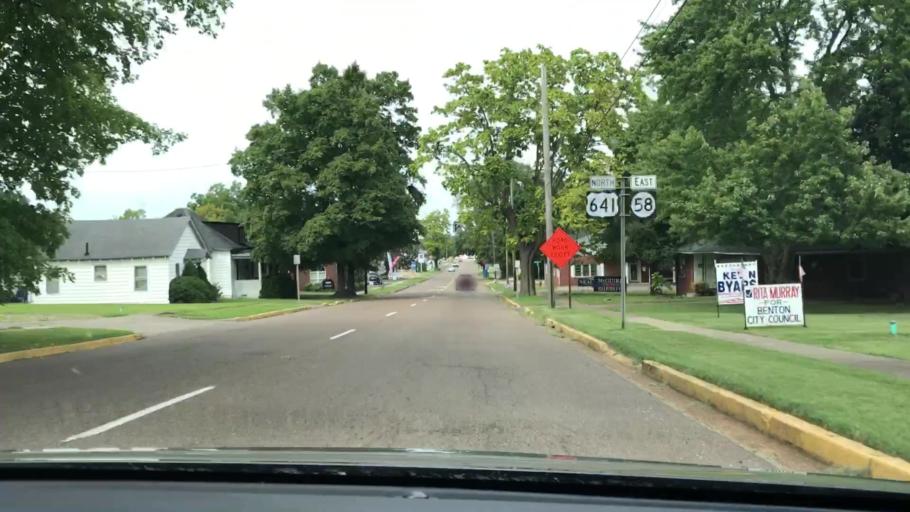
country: US
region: Kentucky
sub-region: Marshall County
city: Benton
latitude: 36.8593
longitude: -88.3499
